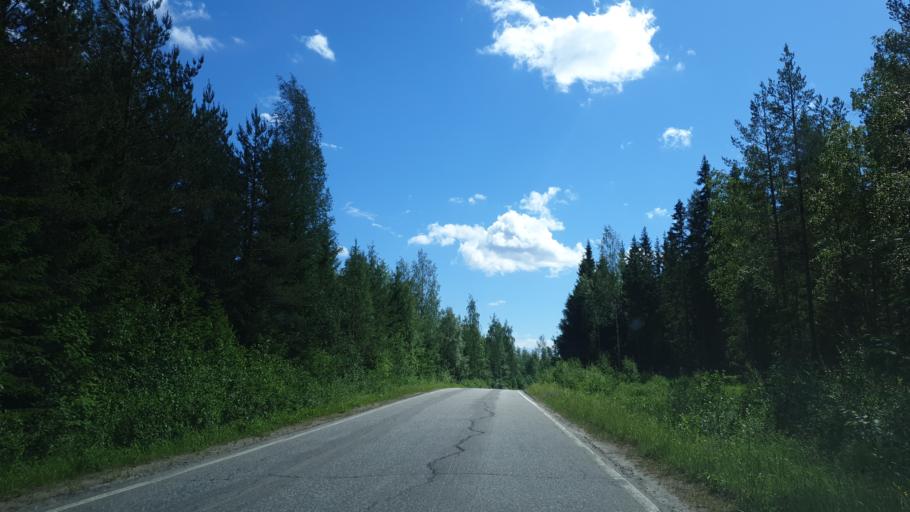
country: FI
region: Northern Savo
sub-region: Koillis-Savo
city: Kaavi
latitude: 63.0005
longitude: 28.5023
